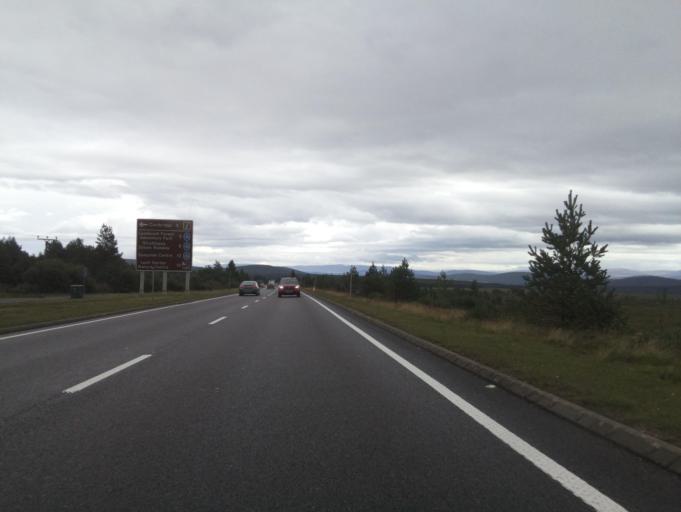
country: GB
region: Scotland
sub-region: Highland
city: Aviemore
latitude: 57.2914
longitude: -3.8883
